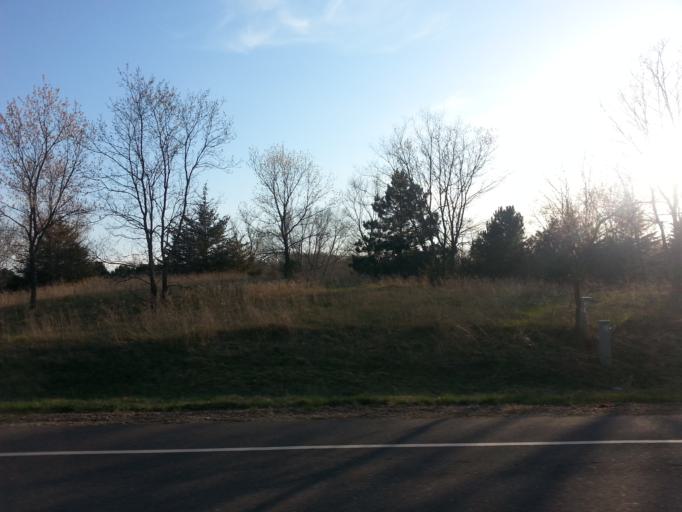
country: US
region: Minnesota
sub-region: Washington County
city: Lake Saint Croix Beach
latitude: 44.9186
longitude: -92.6861
